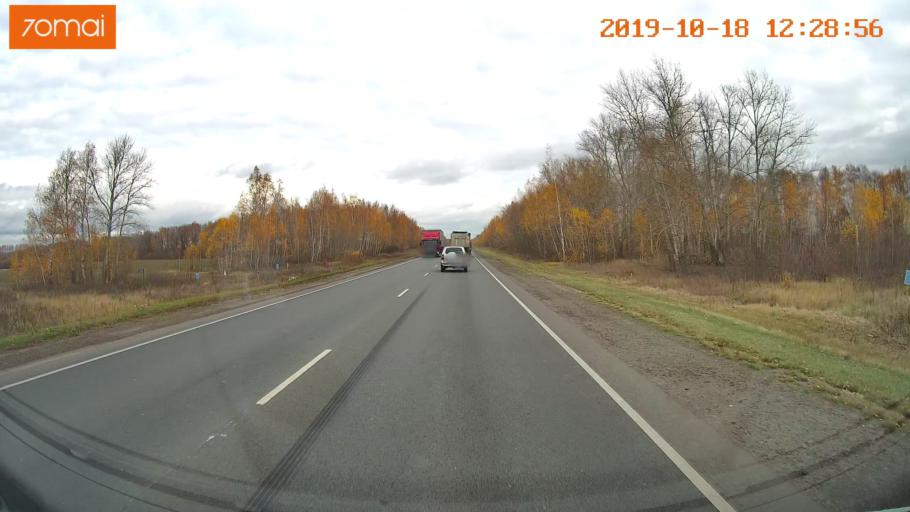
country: RU
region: Rjazan
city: Ryazan'
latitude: 54.5754
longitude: 39.5765
